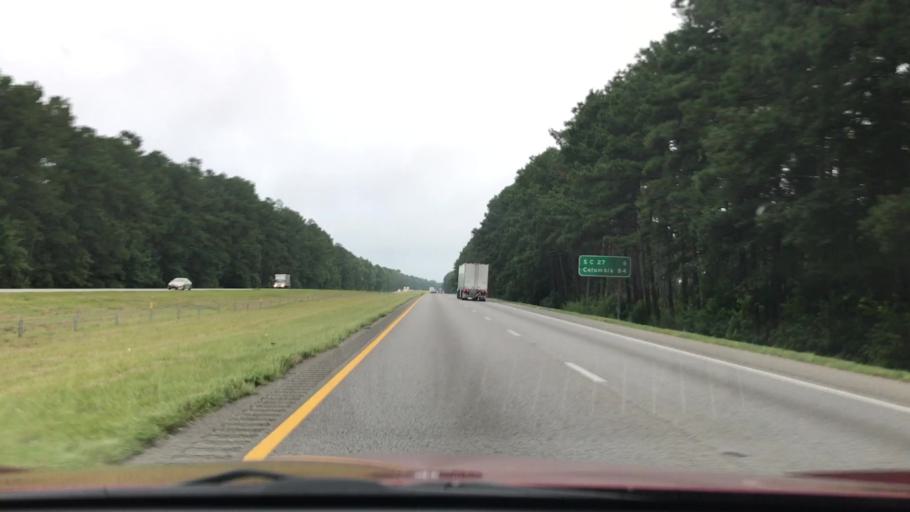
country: US
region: South Carolina
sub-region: Dorchester County
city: Summerville
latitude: 33.0876
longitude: -80.2181
